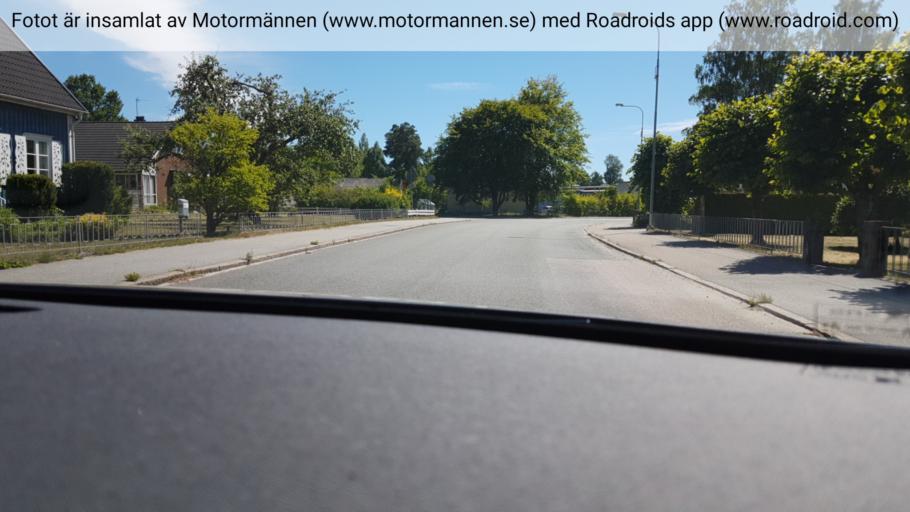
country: SE
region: Joenkoeping
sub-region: Gnosjo Kommun
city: Hillerstorp
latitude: 57.3127
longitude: 13.8798
